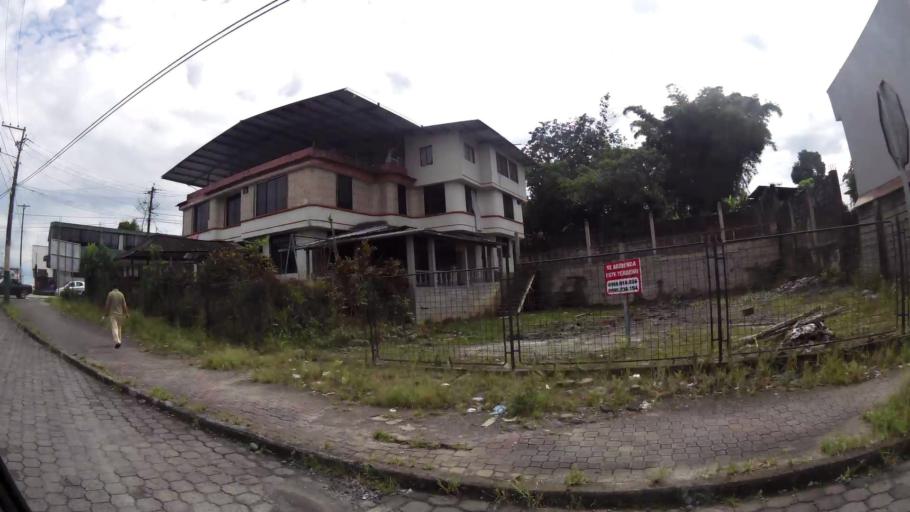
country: EC
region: Pastaza
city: Puyo
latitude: -1.4963
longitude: -78.0008
